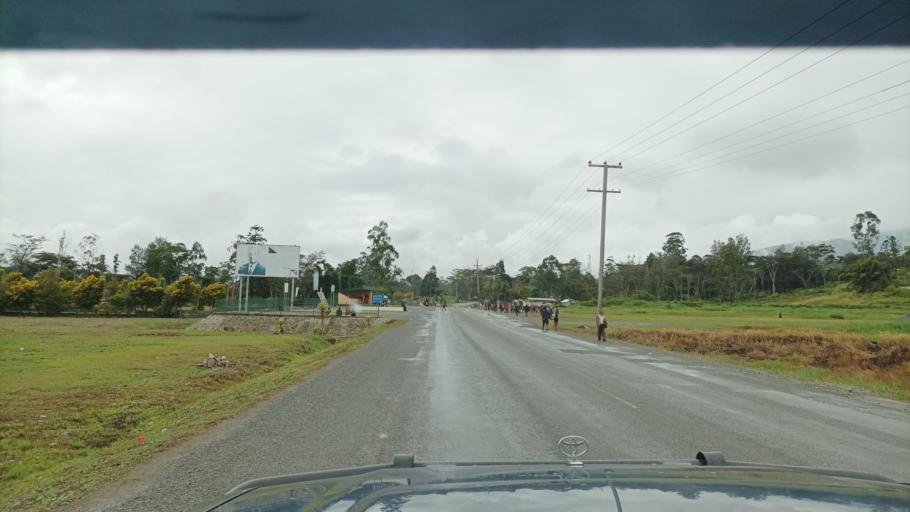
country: PG
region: Jiwaka
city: Minj
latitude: -5.8516
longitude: 144.6265
